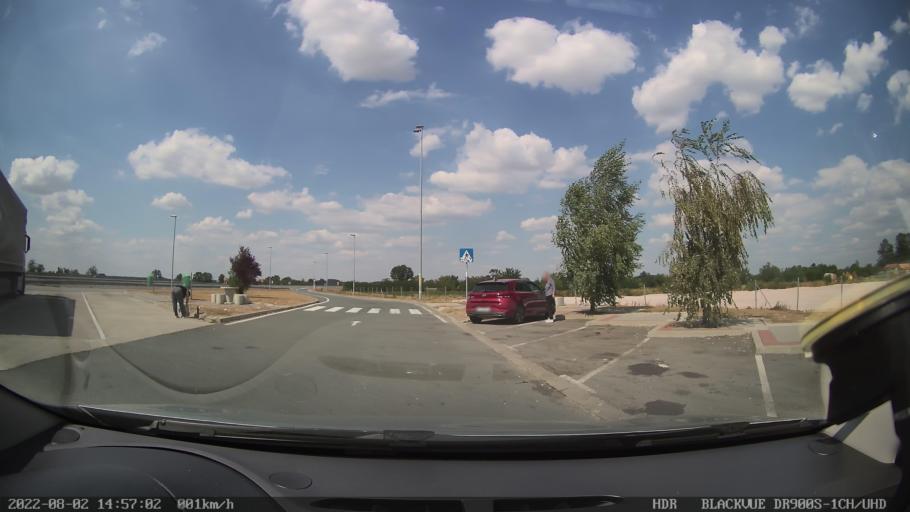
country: RS
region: Central Serbia
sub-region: Kolubarski Okrug
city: Ub
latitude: 44.4060
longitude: 20.0954
